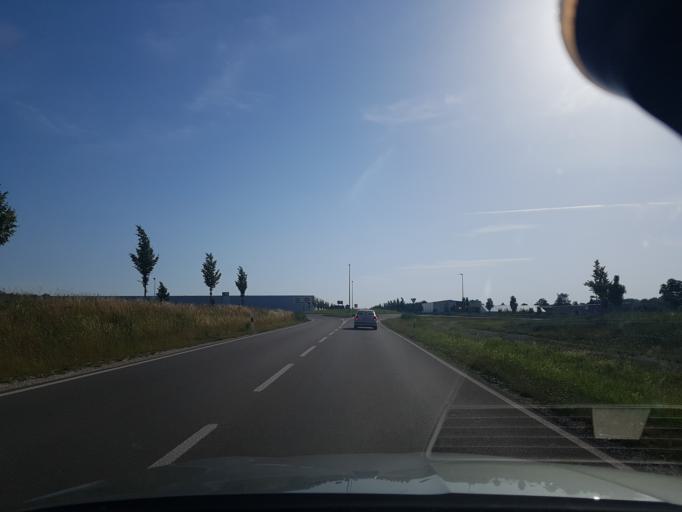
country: DE
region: Bavaria
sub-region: Swabia
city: Bubesheim
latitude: 48.4412
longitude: 10.2384
